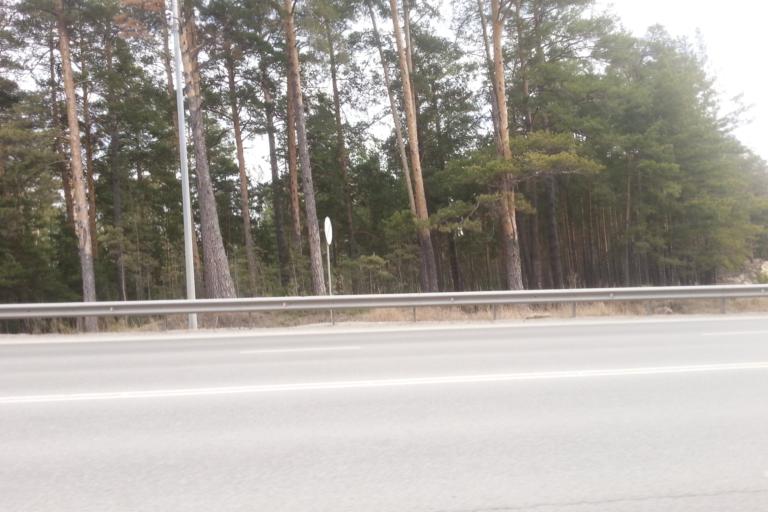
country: RU
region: Altai Krai
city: Yuzhnyy
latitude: 53.3175
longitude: 83.7059
